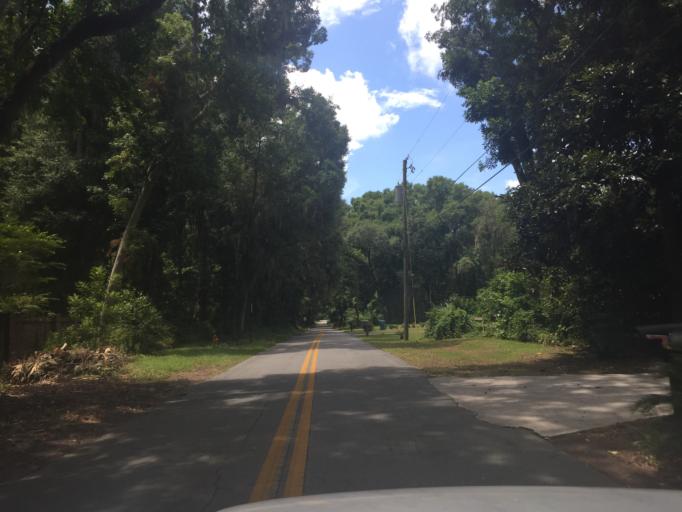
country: US
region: Georgia
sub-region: Chatham County
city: Montgomery
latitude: 31.9478
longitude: -81.1051
